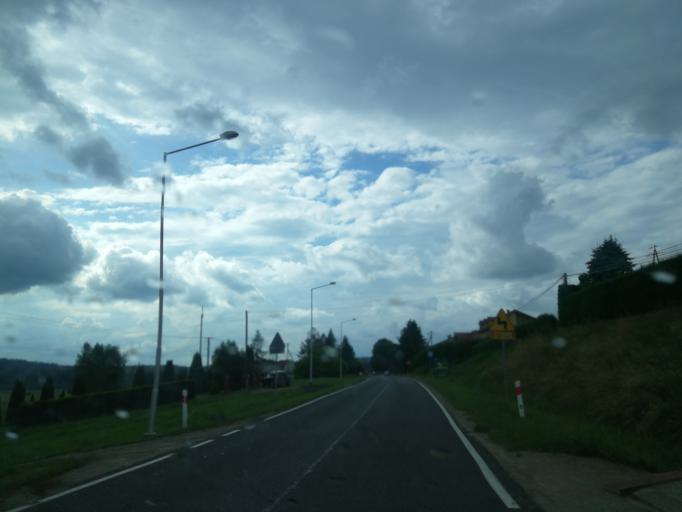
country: PL
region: Subcarpathian Voivodeship
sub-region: Powiat leski
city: Uherce Mineralne
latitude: 49.4561
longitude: 22.4170
